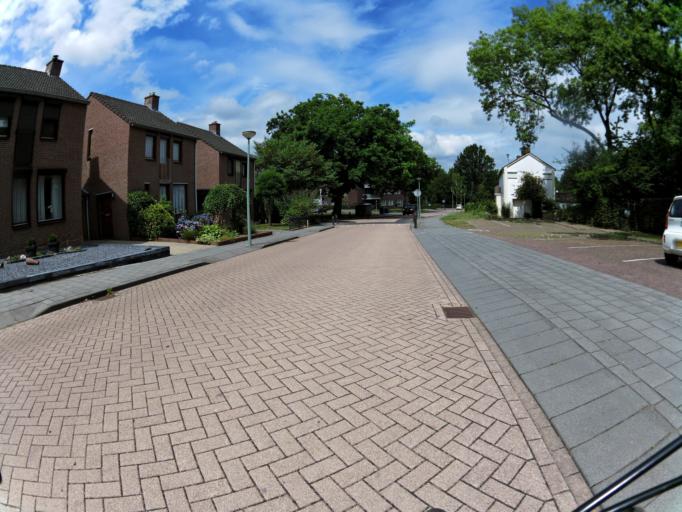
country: NL
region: Limburg
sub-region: Gemeente Brunssum
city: Brunssum
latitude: 50.9407
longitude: 5.9760
